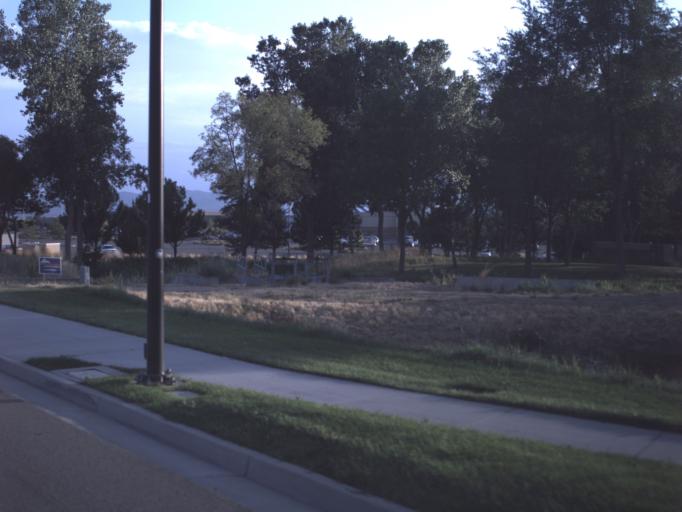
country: US
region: Utah
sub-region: Salt Lake County
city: White City
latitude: 40.5647
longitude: -111.8910
